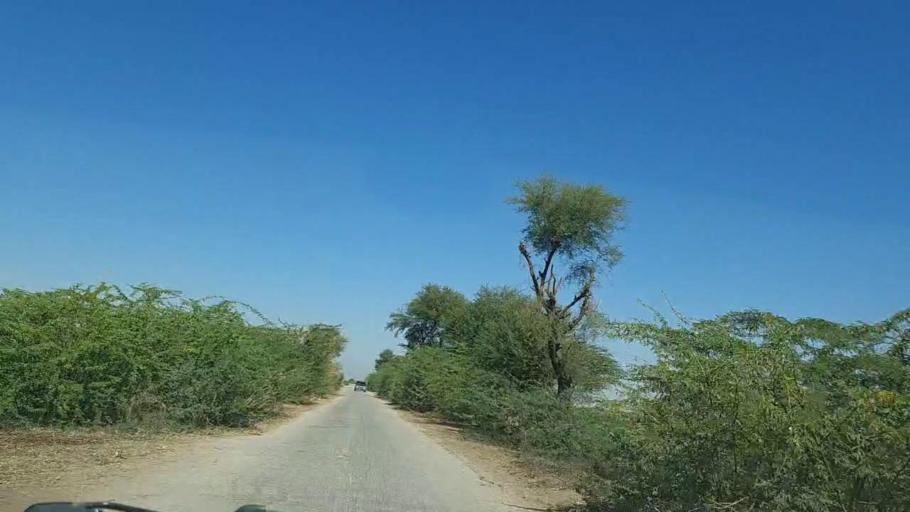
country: PK
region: Sindh
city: Dhoro Naro
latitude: 25.4700
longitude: 69.5262
